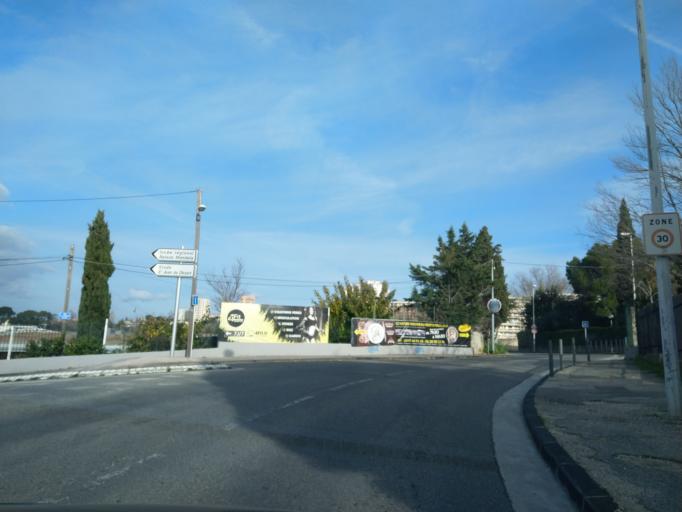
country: FR
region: Provence-Alpes-Cote d'Azur
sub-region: Departement des Bouches-du-Rhone
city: Marseille 12
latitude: 43.2974
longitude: 5.4277
